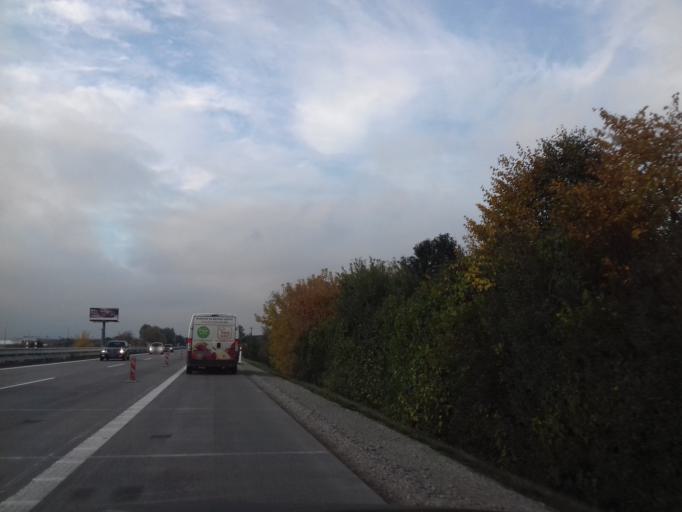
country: CZ
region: South Moravian
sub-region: Okres Brno-Venkov
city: Blucina
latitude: 49.0521
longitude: 16.6732
